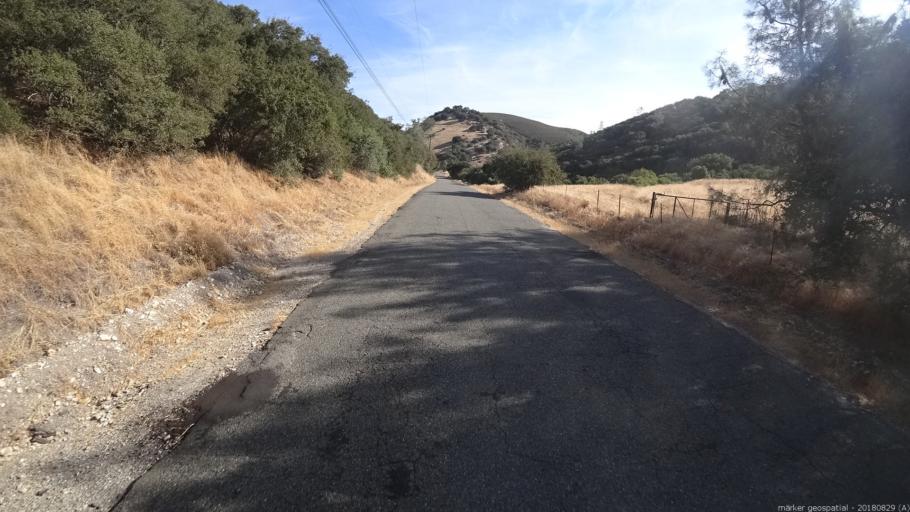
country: US
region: California
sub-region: Monterey County
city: King City
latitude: 35.9990
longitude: -121.0688
